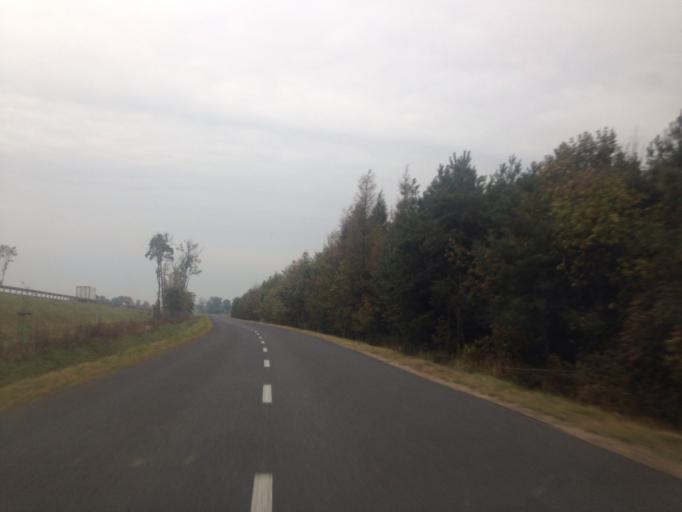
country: PL
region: Greater Poland Voivodeship
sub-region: Powiat gnieznienski
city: Lubowo
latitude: 52.4831
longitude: 17.4202
